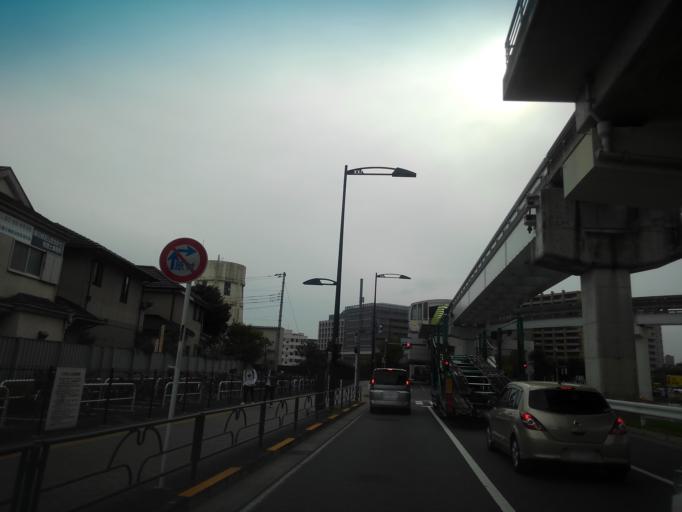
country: JP
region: Tokyo
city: Hino
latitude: 35.7112
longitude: 139.4143
